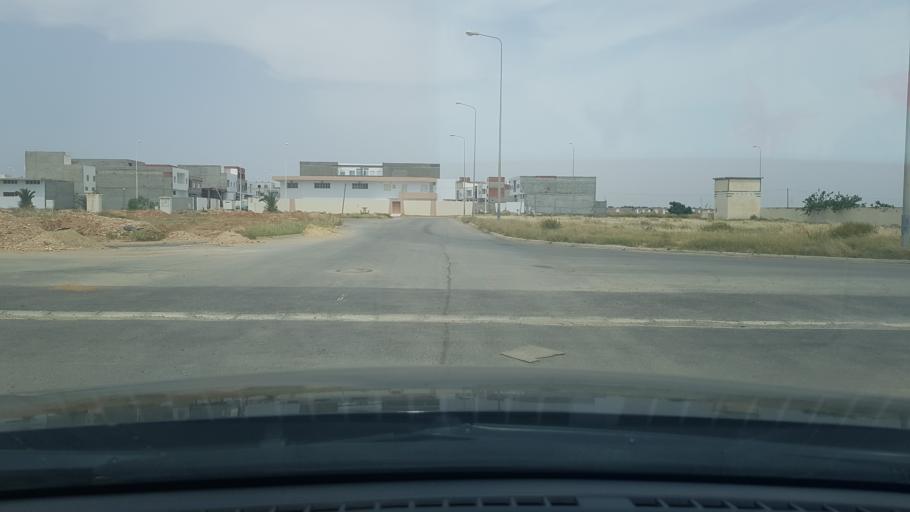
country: TN
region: Safaqis
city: Al Qarmadah
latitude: 34.8243
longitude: 10.7427
